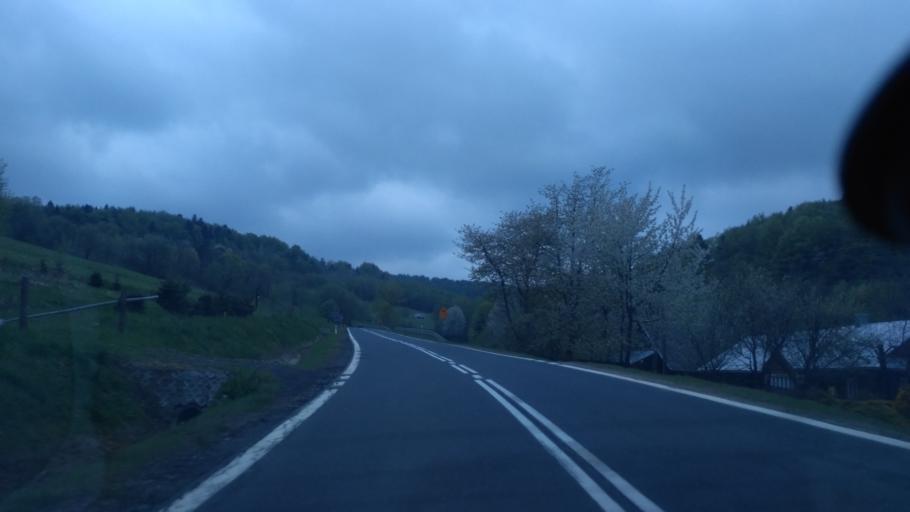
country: PL
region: Subcarpathian Voivodeship
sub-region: Powiat sanocki
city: Tyrawa Woloska
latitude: 49.5692
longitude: 22.3501
